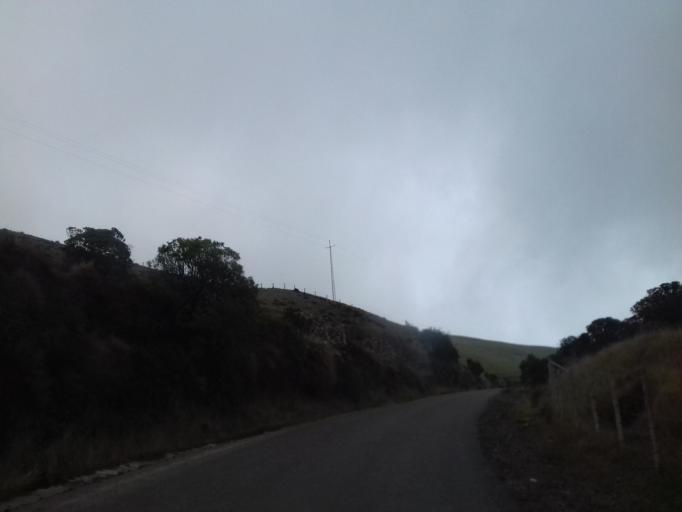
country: CO
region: Caldas
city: Villamaria
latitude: 4.9753
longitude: -75.3397
